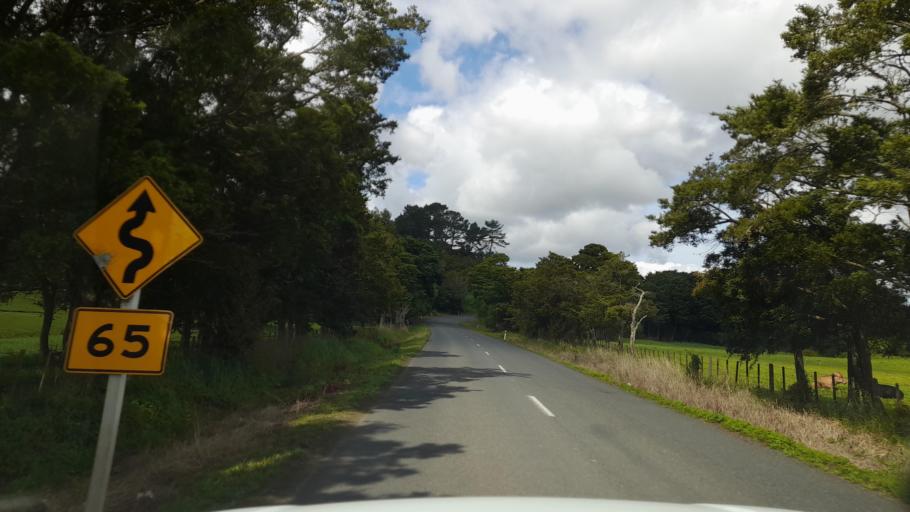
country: NZ
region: Northland
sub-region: Whangarei
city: Maungatapere
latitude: -35.6513
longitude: 174.1436
